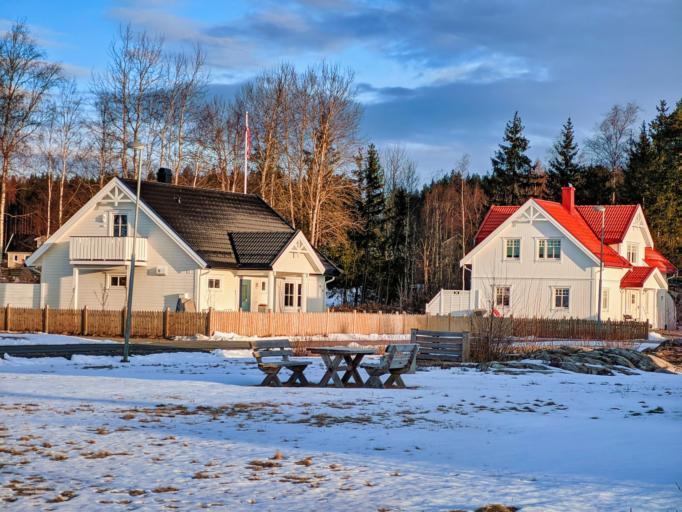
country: NO
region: Akershus
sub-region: Nes
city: Arnes
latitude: 60.1702
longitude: 11.5438
